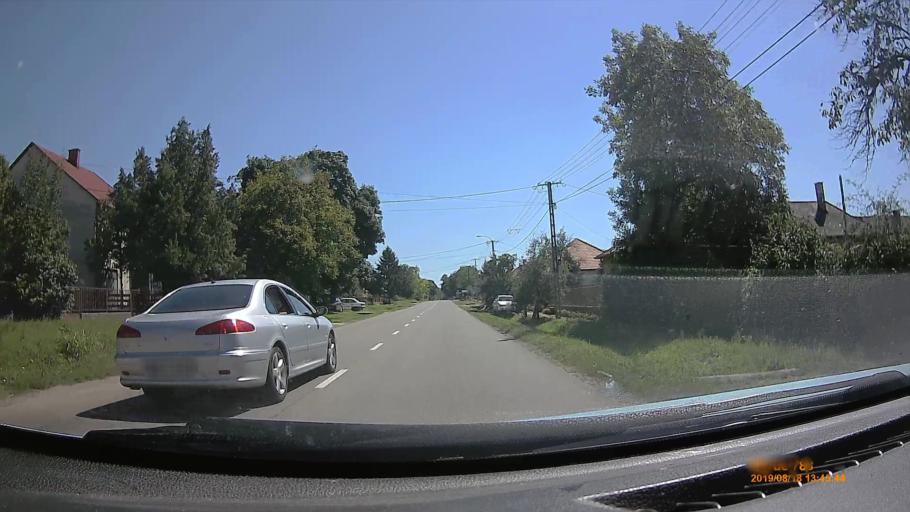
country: HU
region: Fejer
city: Cece
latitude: 46.7561
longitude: 18.6392
